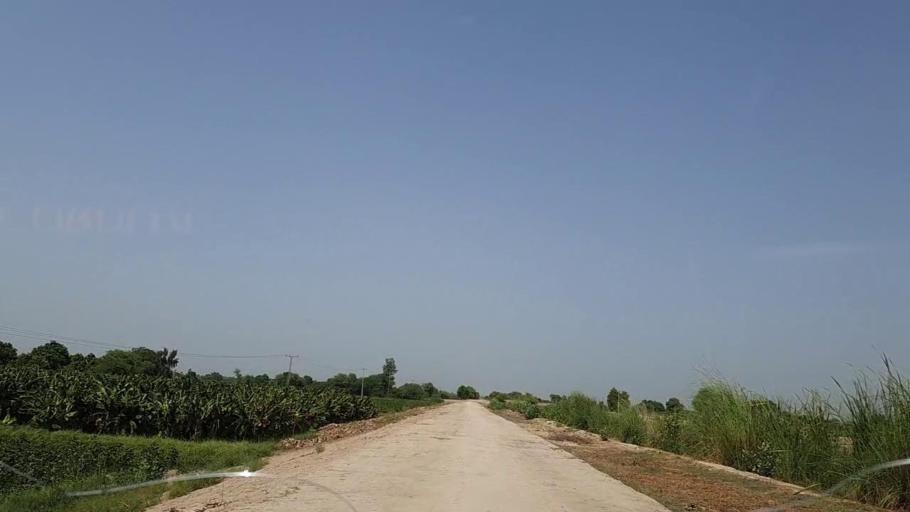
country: PK
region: Sindh
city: Kandiaro
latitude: 27.0323
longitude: 68.1471
